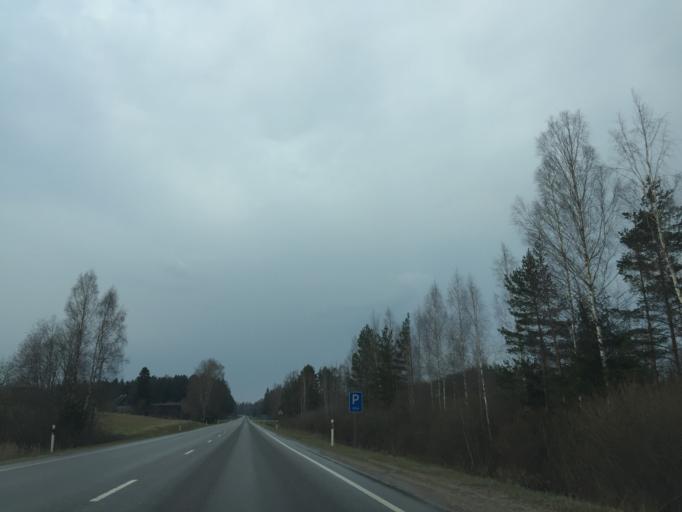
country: EE
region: Tartu
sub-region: UElenurme vald
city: Ulenurme
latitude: 58.1122
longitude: 26.7363
